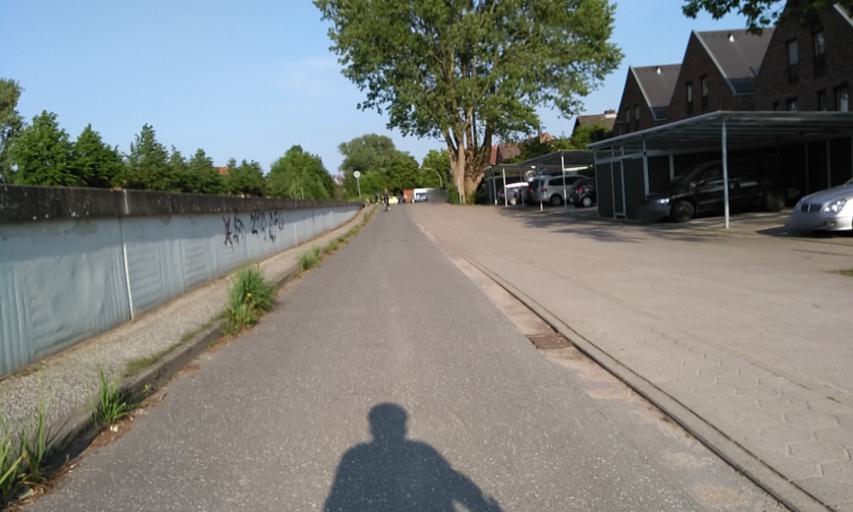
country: DE
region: Hamburg
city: Altona
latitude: 53.5346
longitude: 9.8712
